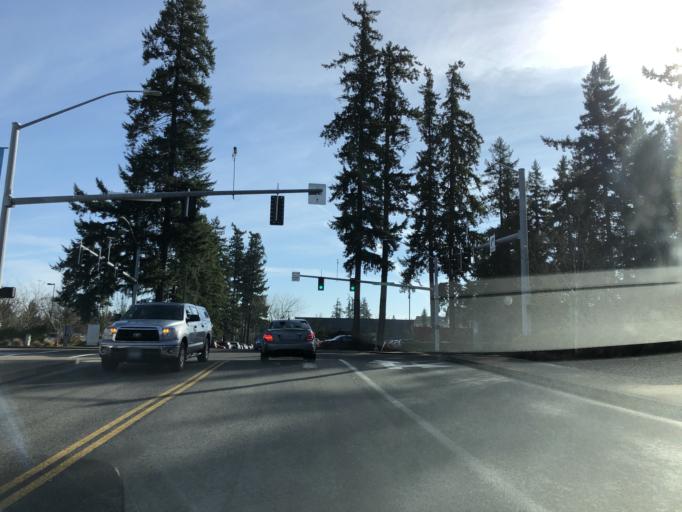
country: US
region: Oregon
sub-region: Washington County
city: Durham
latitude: 45.3944
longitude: -122.7534
